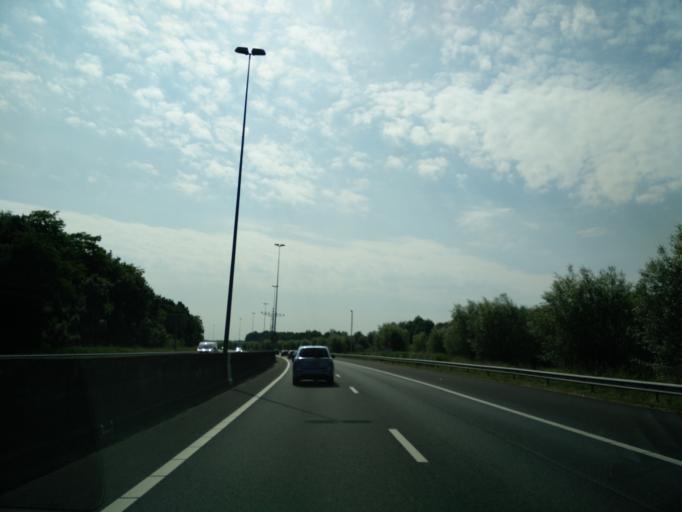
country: NL
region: Groningen
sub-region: Gemeente Groningen
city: Groningen
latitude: 53.1872
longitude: 6.5679
